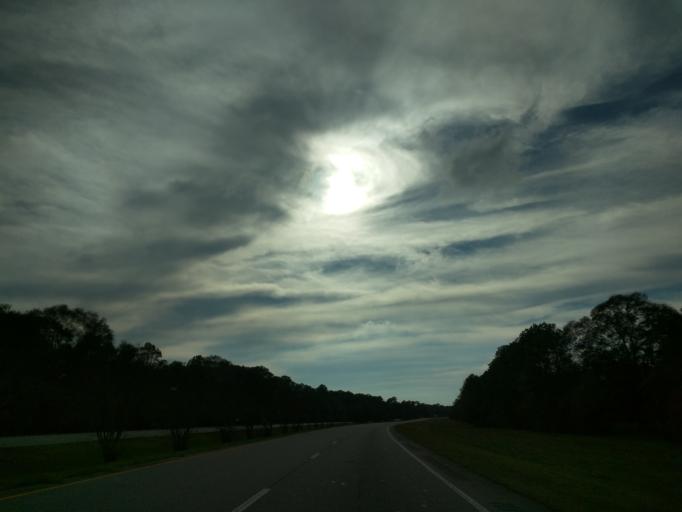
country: US
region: Georgia
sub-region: Decatur County
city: Bainbridge
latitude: 30.8961
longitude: -84.5498
